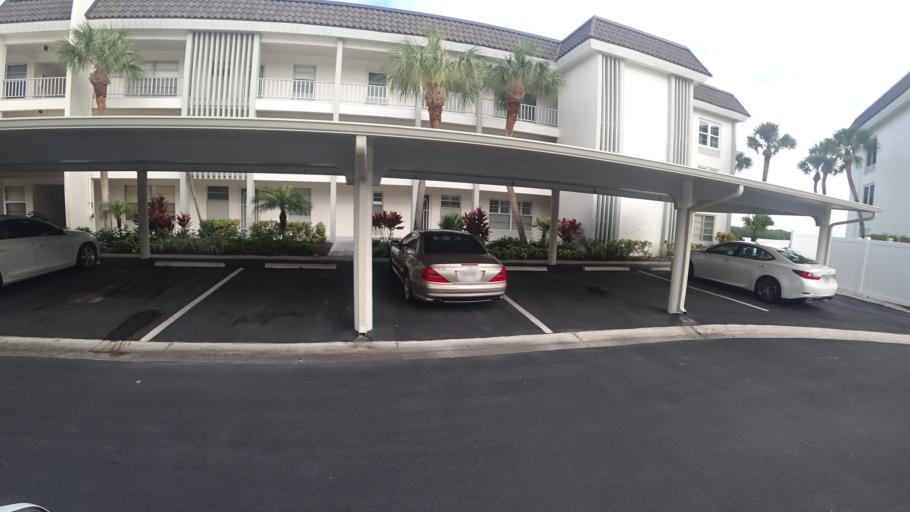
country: US
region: Florida
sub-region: Manatee County
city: Longboat Key
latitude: 27.3965
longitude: -82.6446
